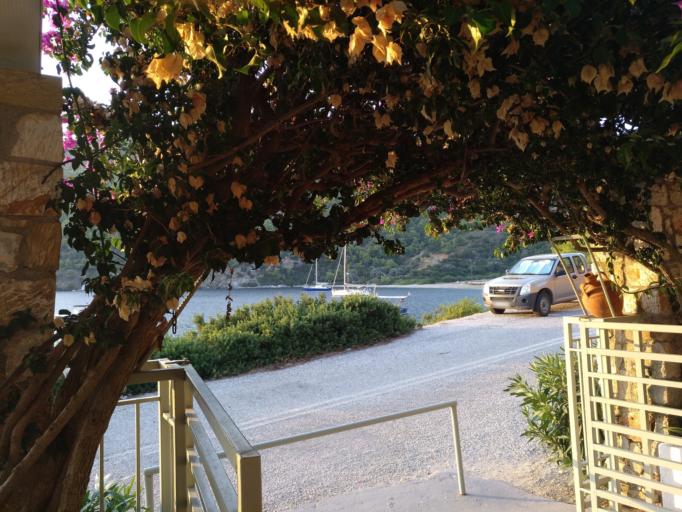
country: GR
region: Central Greece
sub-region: Nomos Evvoias
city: Skyros
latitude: 38.8543
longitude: 24.5105
